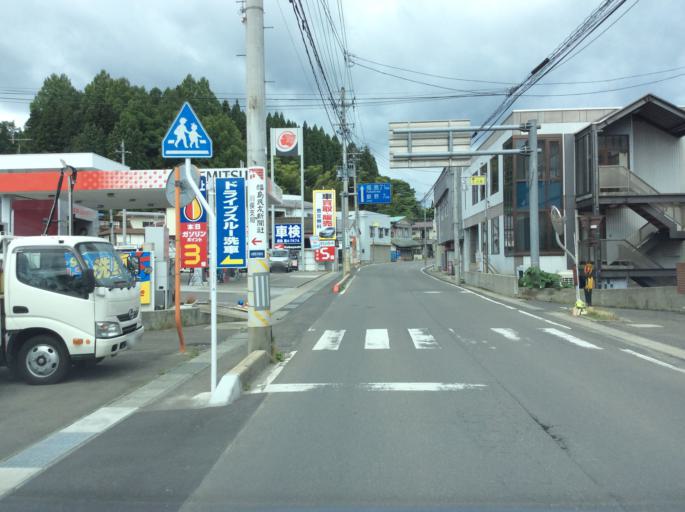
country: JP
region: Fukushima
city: Fukushima-shi
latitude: 37.6631
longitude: 140.6018
